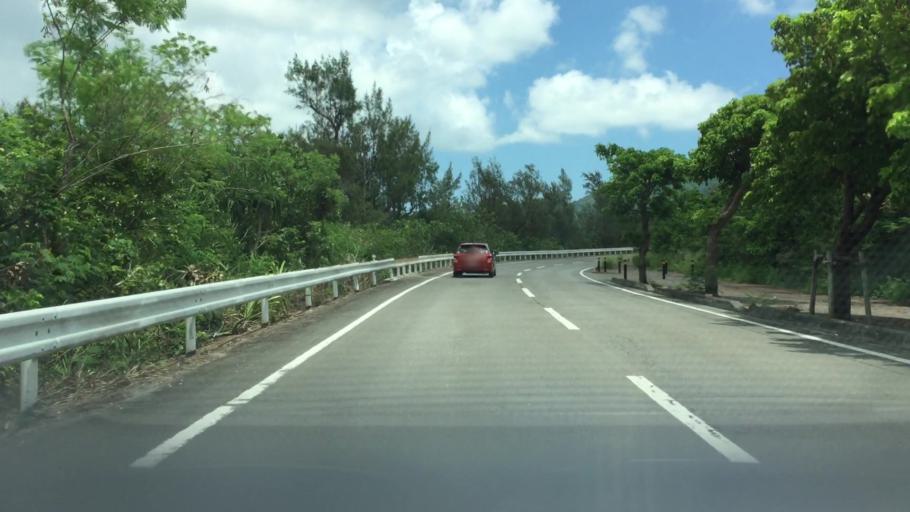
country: JP
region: Okinawa
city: Ishigaki
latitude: 24.3998
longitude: 124.1403
